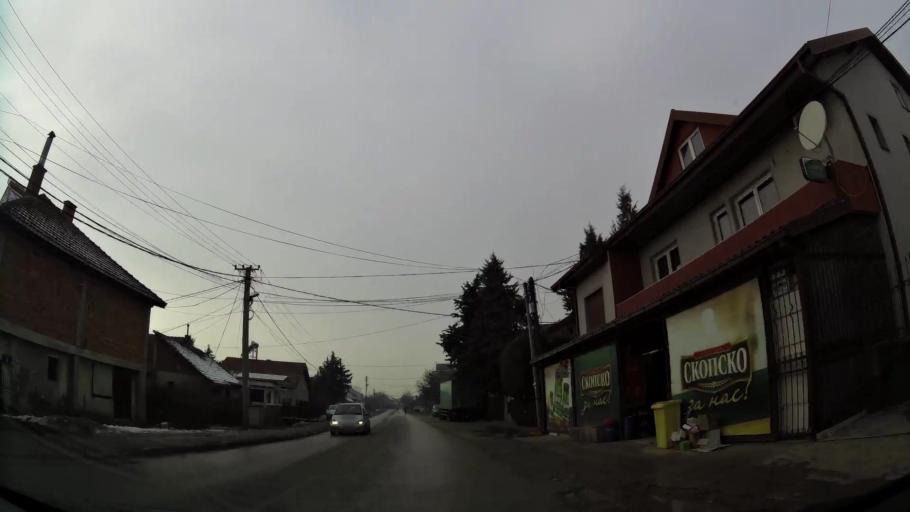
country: MK
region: Ilinden
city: Ilinden
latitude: 41.9971
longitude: 21.5770
